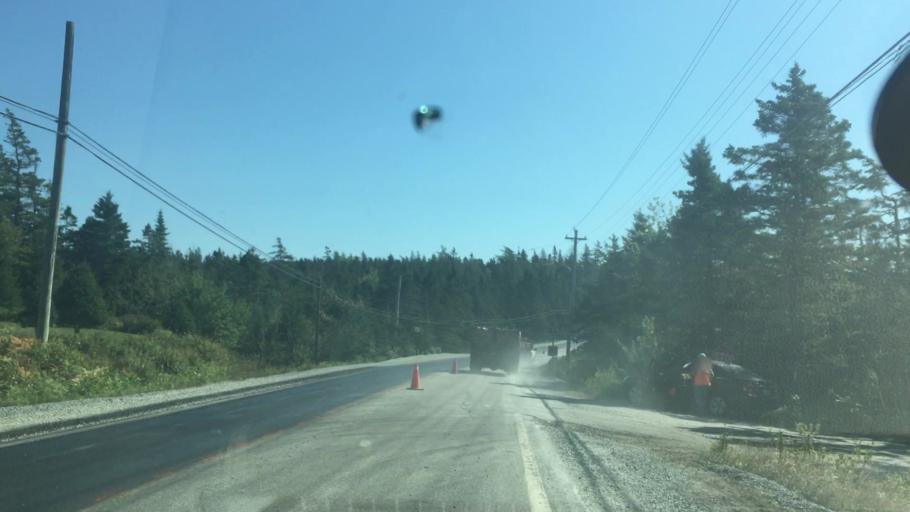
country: CA
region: Nova Scotia
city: New Glasgow
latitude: 44.9070
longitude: -62.4937
